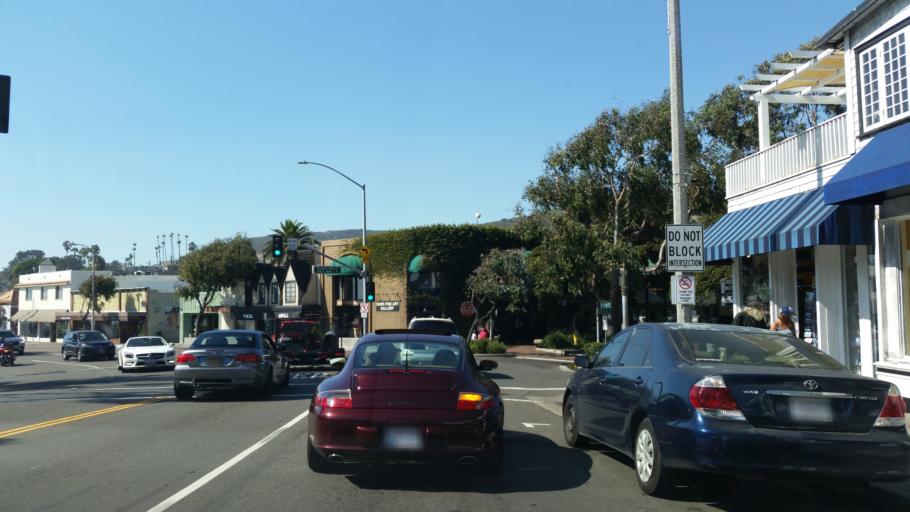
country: US
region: California
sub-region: Orange County
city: Laguna Beach
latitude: 33.5419
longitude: -117.7831
